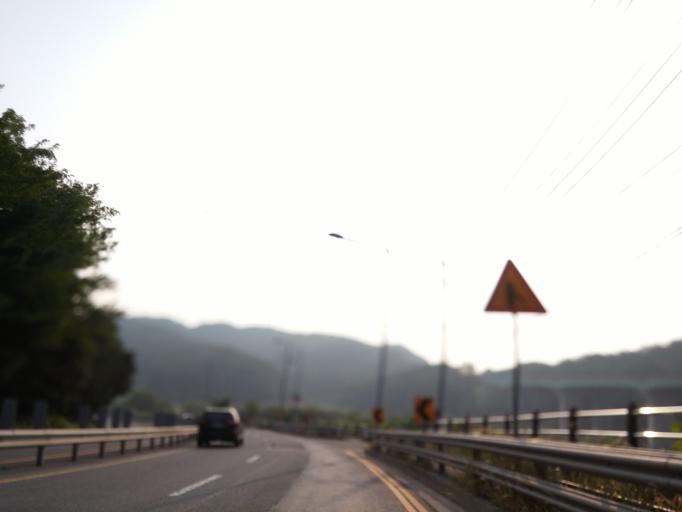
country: KR
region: Daejeon
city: Daejeon
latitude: 36.3476
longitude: 127.4945
